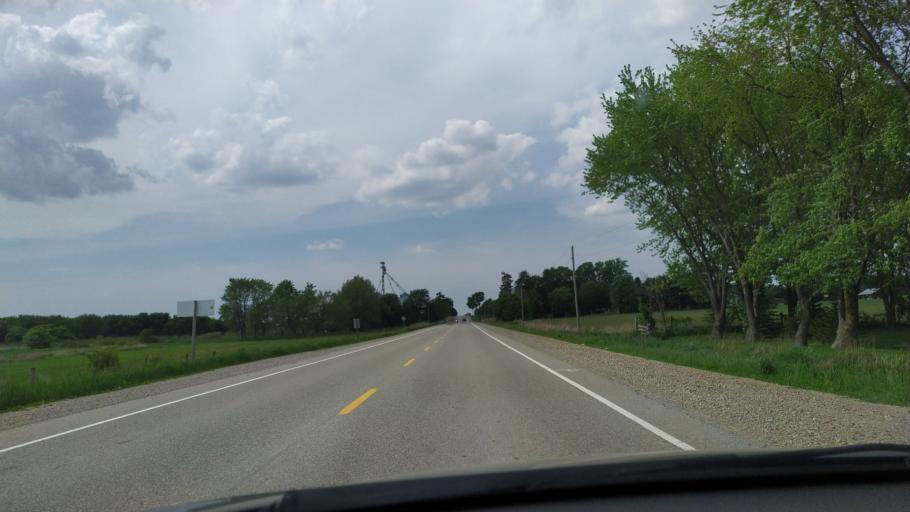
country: CA
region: Ontario
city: Dorchester
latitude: 43.1653
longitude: -81.0435
